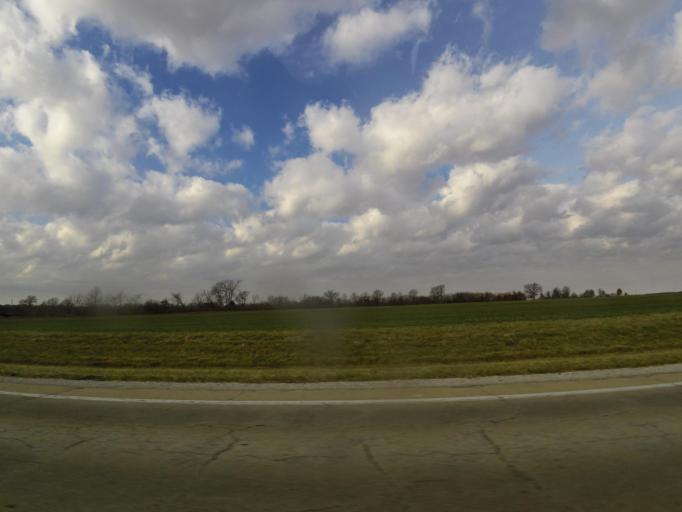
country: US
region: Illinois
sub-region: Fayette County
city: Ramsey
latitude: 39.1995
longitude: -89.1009
